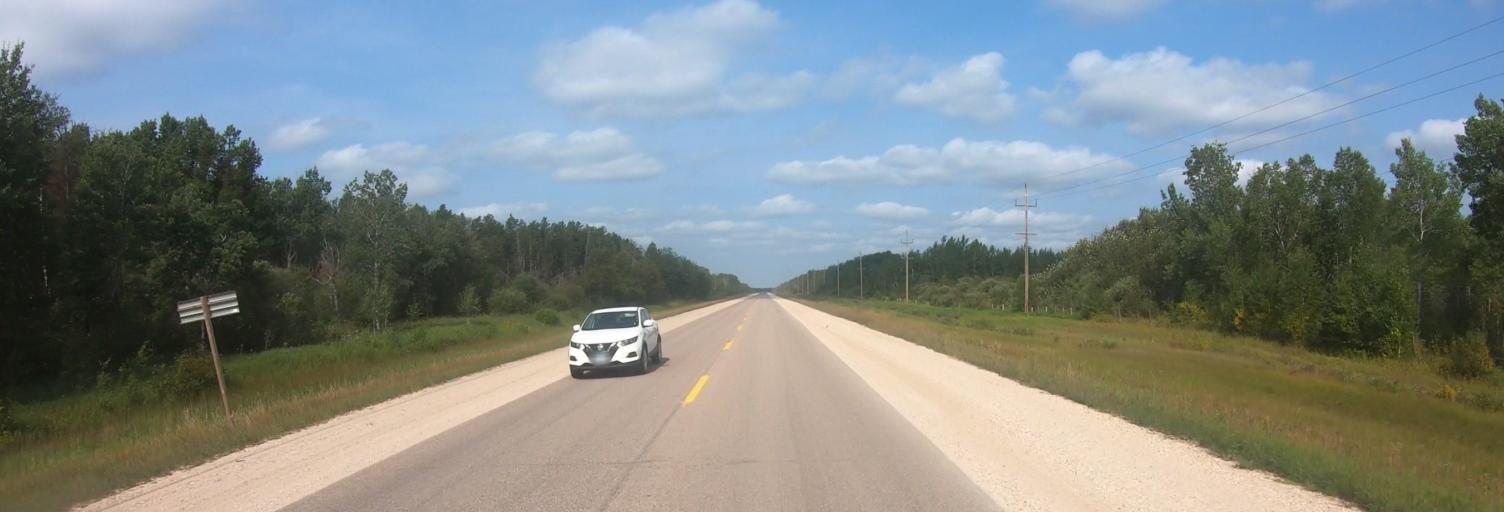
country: CA
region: Manitoba
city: La Broquerie
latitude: 49.2226
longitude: -96.3090
